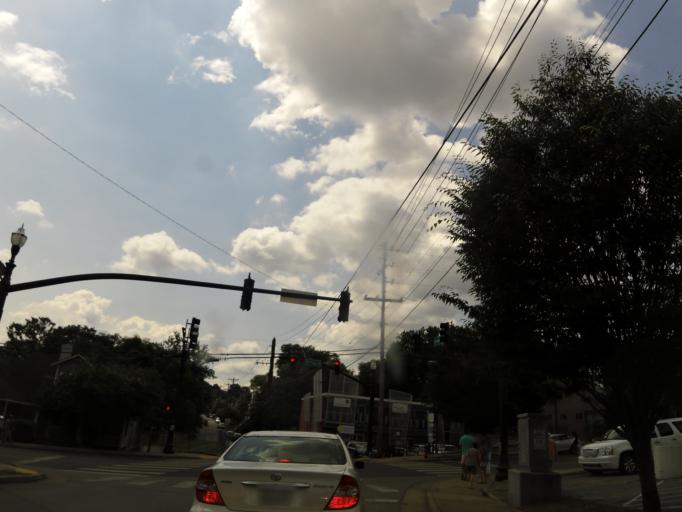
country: US
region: Tennessee
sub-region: Davidson County
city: Oak Hill
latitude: 36.1207
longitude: -86.7903
